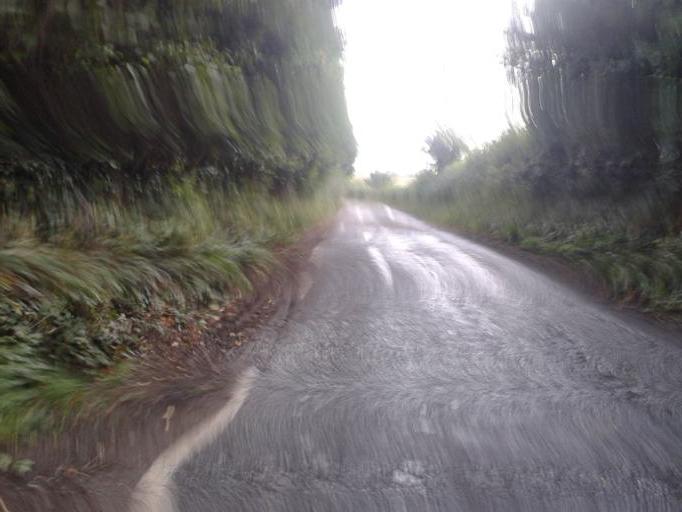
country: GB
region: England
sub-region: Hertfordshire
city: Reed
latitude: 51.9916
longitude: 0.0925
